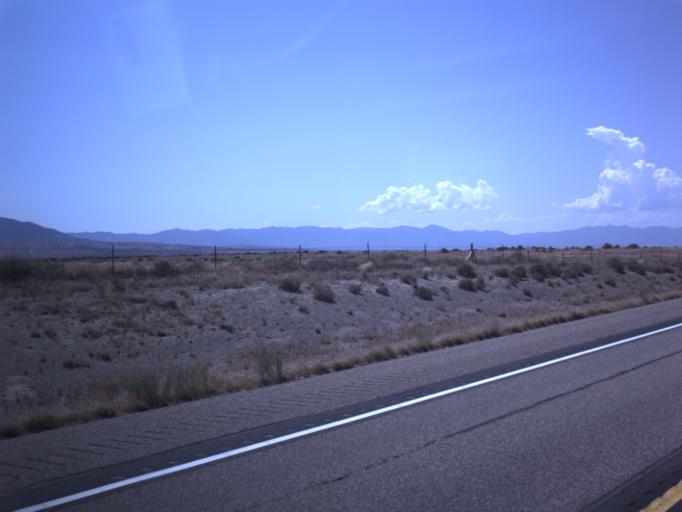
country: US
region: Utah
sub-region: Millard County
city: Delta
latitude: 39.3768
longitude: -112.4965
